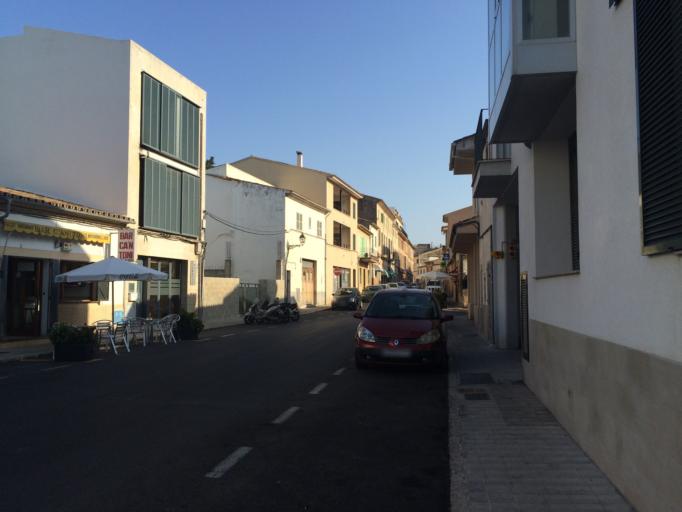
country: ES
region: Balearic Islands
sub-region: Illes Balears
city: Pollenca
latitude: 39.8818
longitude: 3.0194
